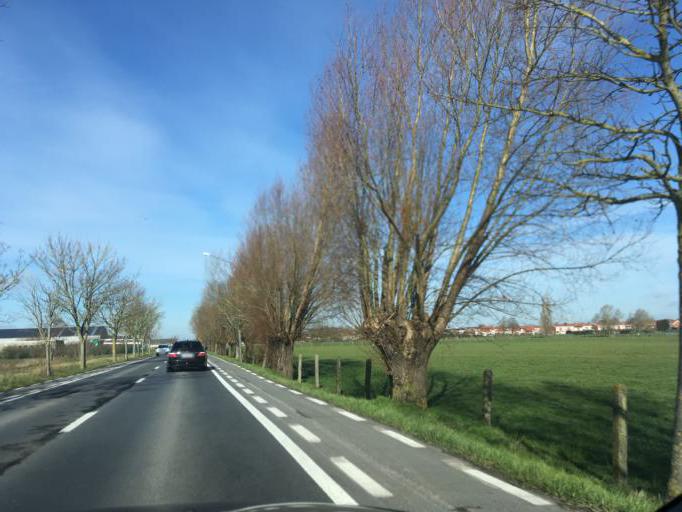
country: BE
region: Flanders
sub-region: Provincie West-Vlaanderen
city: Ledegem
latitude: 50.8502
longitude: 3.1375
